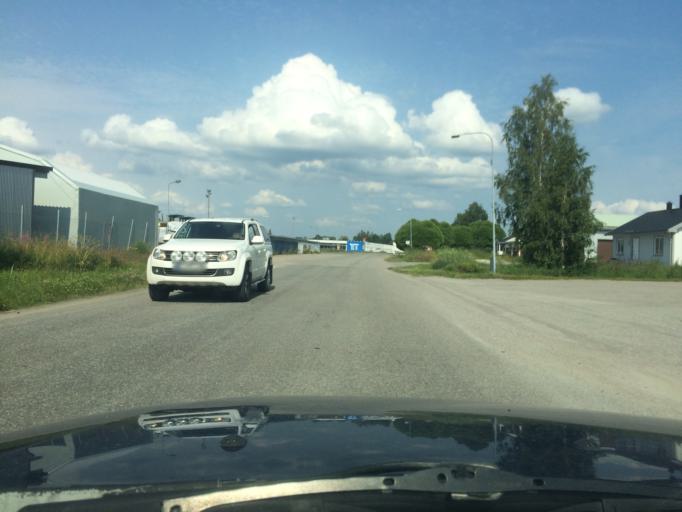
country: SE
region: Norrbotten
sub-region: Pitea Kommun
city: Bergsviken
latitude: 65.3392
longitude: 21.4112
